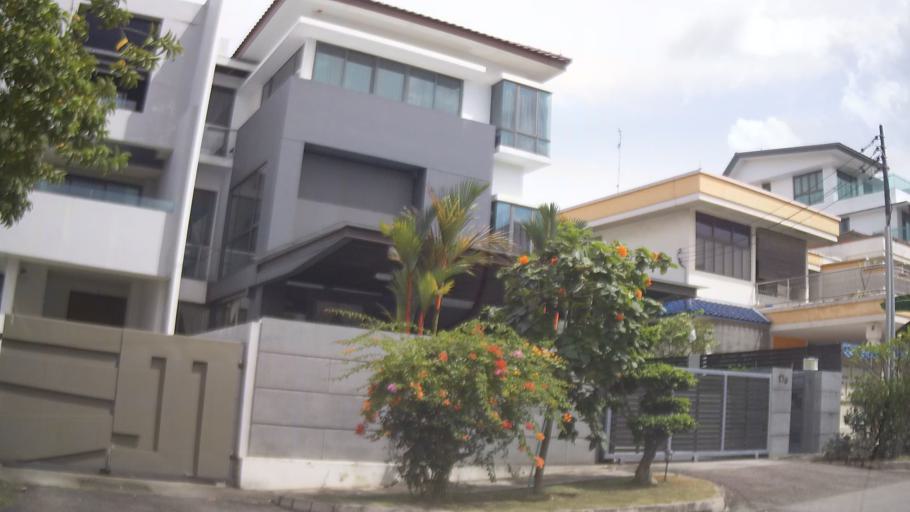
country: SG
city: Singapore
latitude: 1.3503
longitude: 103.8841
